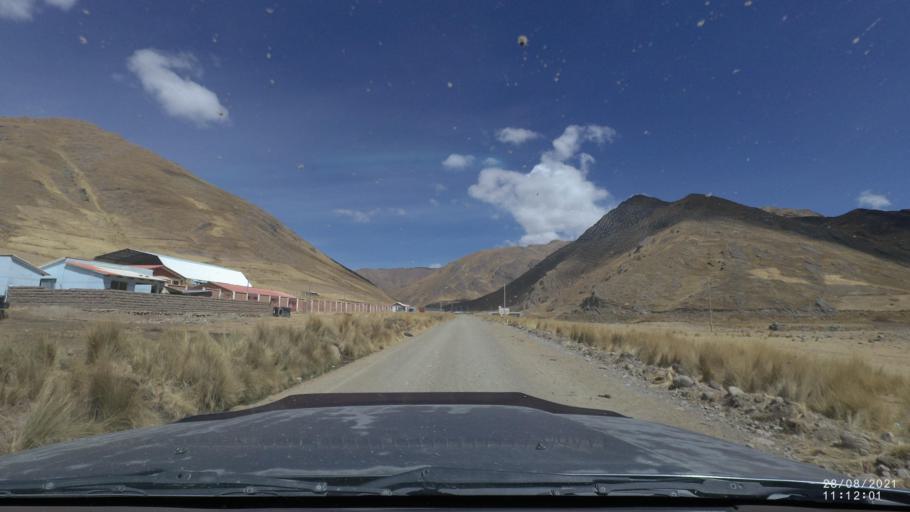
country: BO
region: Cochabamba
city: Cochabamba
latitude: -17.1490
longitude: -66.3162
